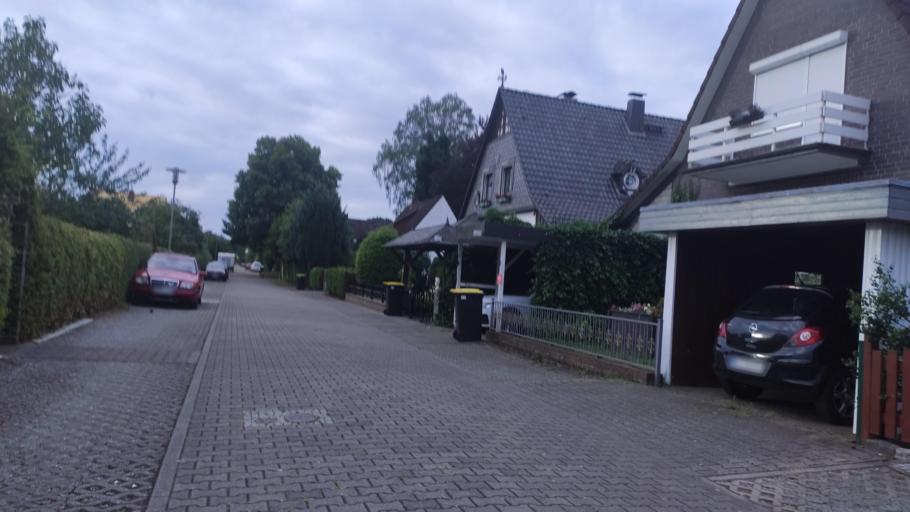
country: DE
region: Schleswig-Holstein
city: Geesthacht
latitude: 53.4426
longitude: 10.3521
